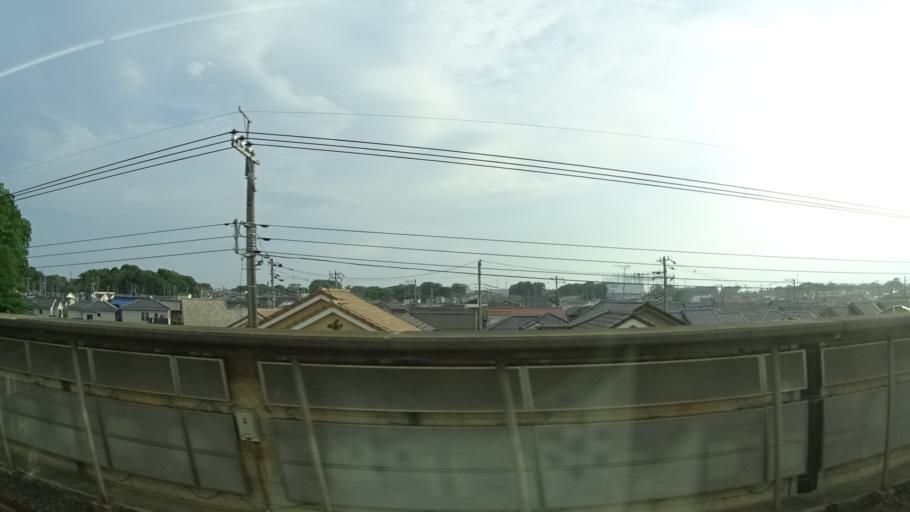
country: JP
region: Saitama
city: Okegawa
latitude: 36.0163
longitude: 139.5971
